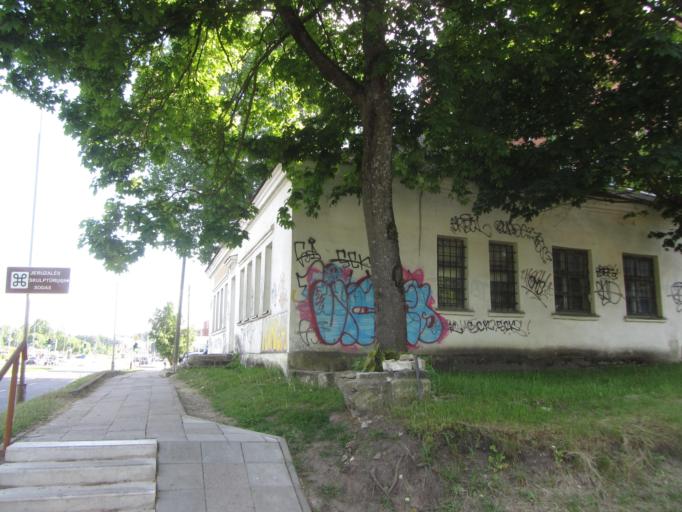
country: LT
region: Vilnius County
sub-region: Vilnius
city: Fabijoniskes
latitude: 54.7456
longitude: 25.2790
